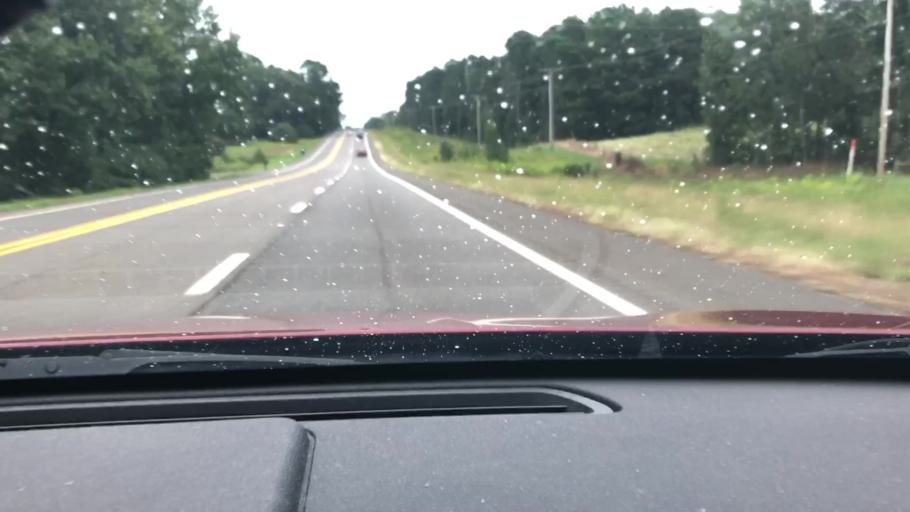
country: US
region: Arkansas
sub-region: Columbia County
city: Waldo
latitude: 33.3512
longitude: -93.3808
